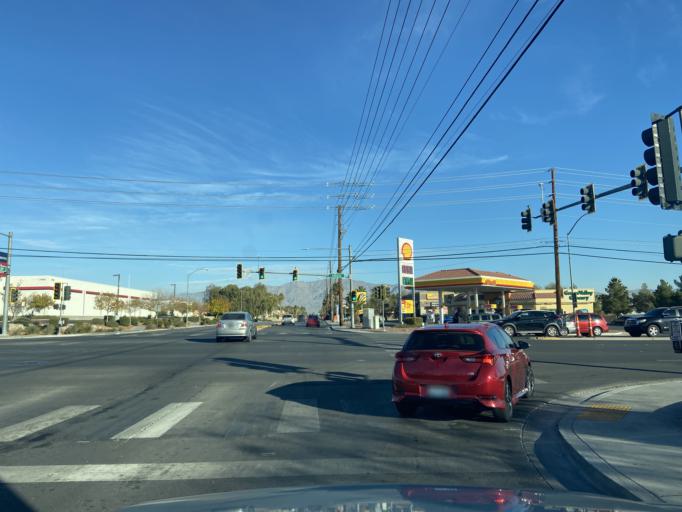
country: US
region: Nevada
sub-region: Clark County
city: North Las Vegas
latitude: 36.2391
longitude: -115.1894
